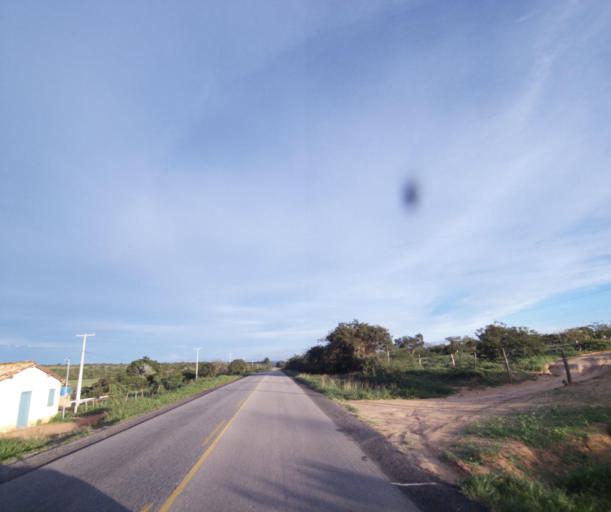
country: BR
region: Bahia
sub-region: Malhada De Pedras
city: Santana
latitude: -14.2189
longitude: -41.9977
